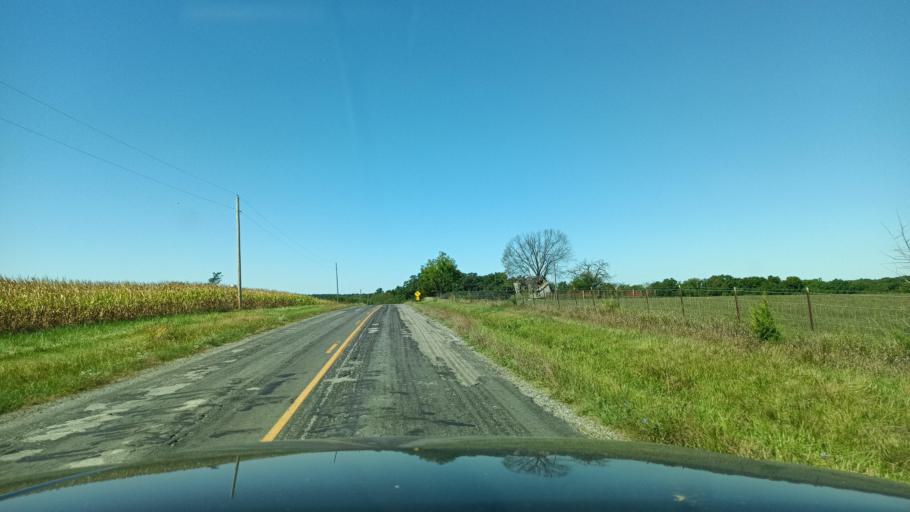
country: US
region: Missouri
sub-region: Scotland County
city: Memphis
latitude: 40.3548
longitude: -92.2317
